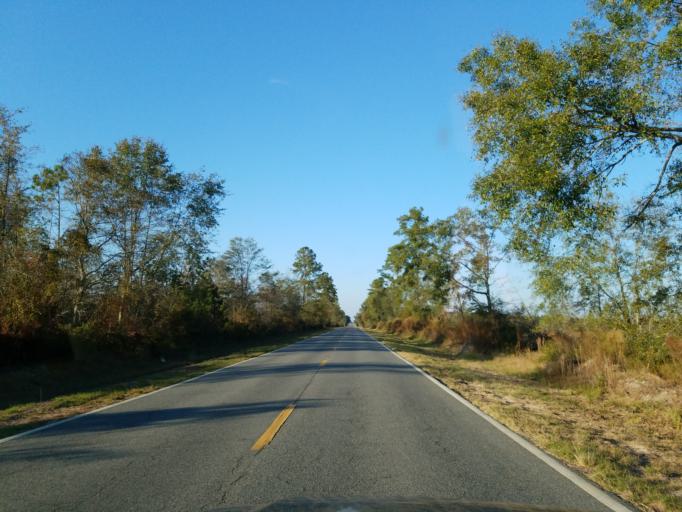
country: US
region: Georgia
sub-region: Lanier County
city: Lakeland
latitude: 31.1505
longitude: -83.0869
